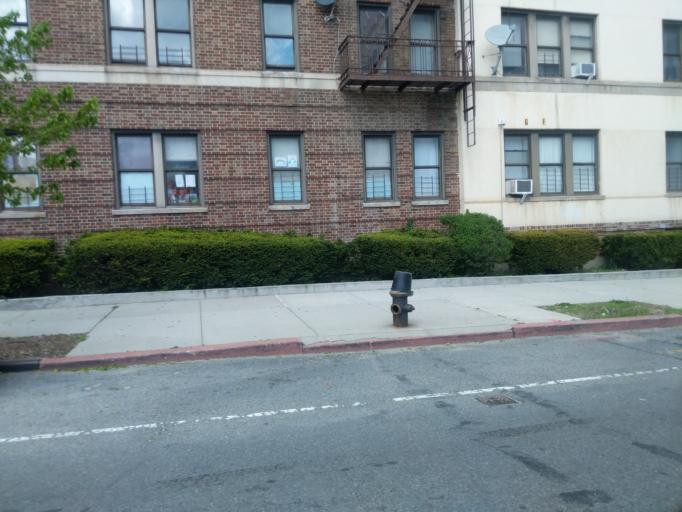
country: US
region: New York
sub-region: Bronx
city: The Bronx
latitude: 40.8772
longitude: -73.8848
